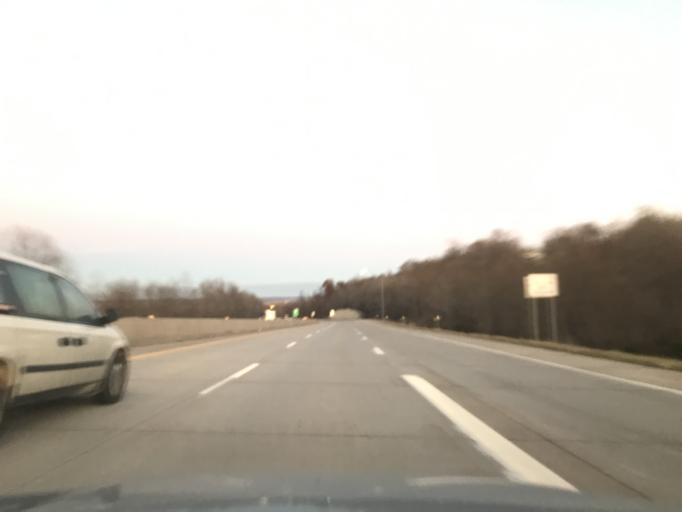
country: US
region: Missouri
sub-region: Marion County
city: Hannibal
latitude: 39.7180
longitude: -91.3676
